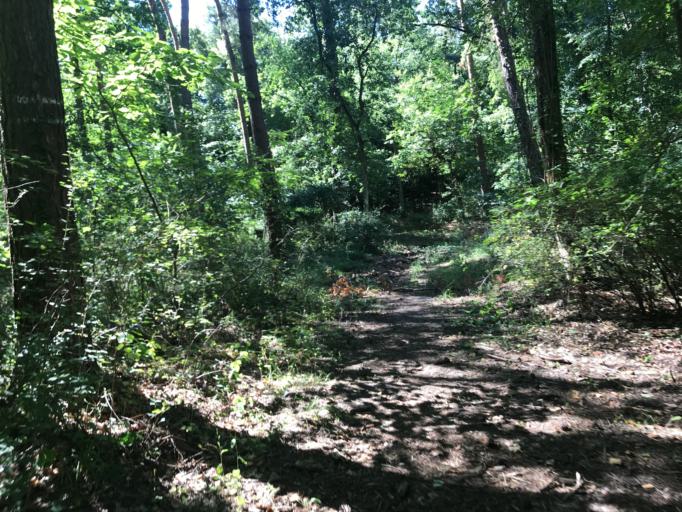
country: DE
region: Rheinland-Pfalz
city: Budenheim
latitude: 50.0153
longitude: 8.1629
